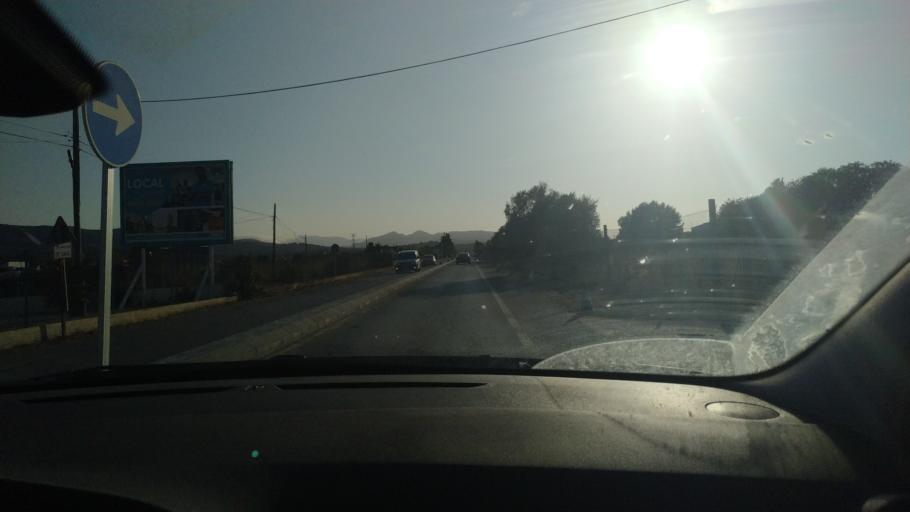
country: ES
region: Valencia
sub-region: Provincia de Alicante
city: Javea
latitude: 38.7754
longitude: 0.1369
